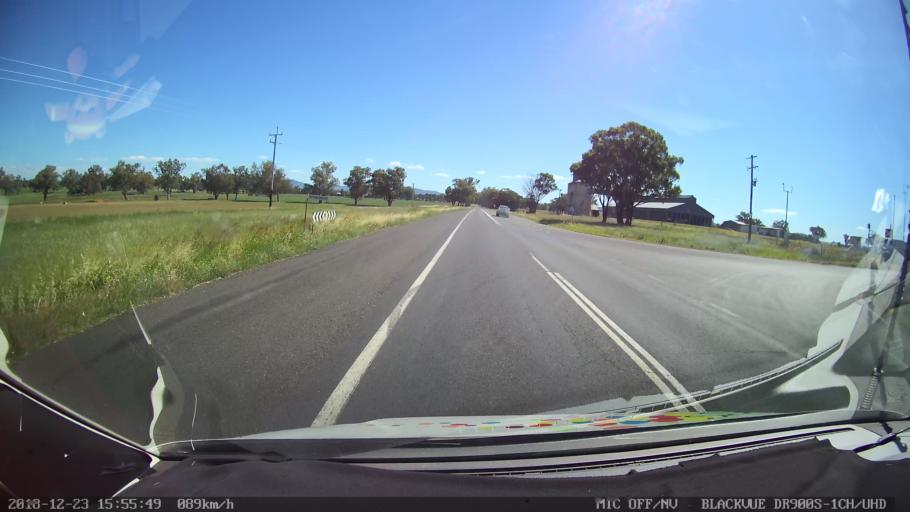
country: AU
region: New South Wales
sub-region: Tamworth Municipality
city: Phillip
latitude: -31.1593
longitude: 150.8646
